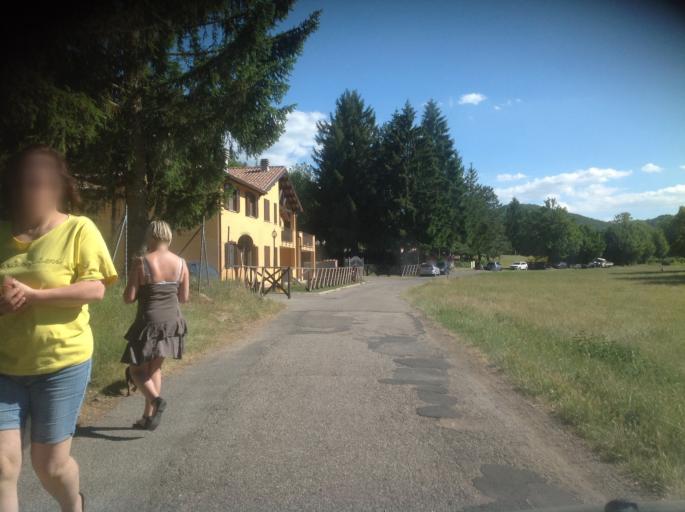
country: IT
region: Latium
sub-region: Provincia di Rieti
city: Limiti di Greccio
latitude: 42.4817
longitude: 12.7146
